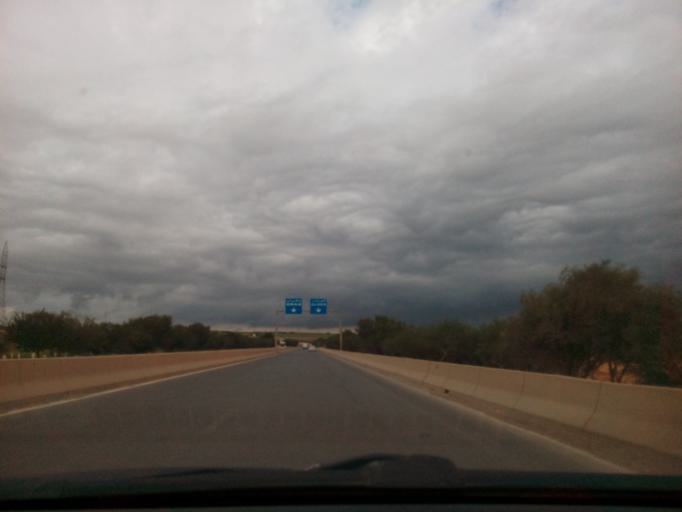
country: DZ
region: Mascara
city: Sig
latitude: 35.5393
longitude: -0.3781
